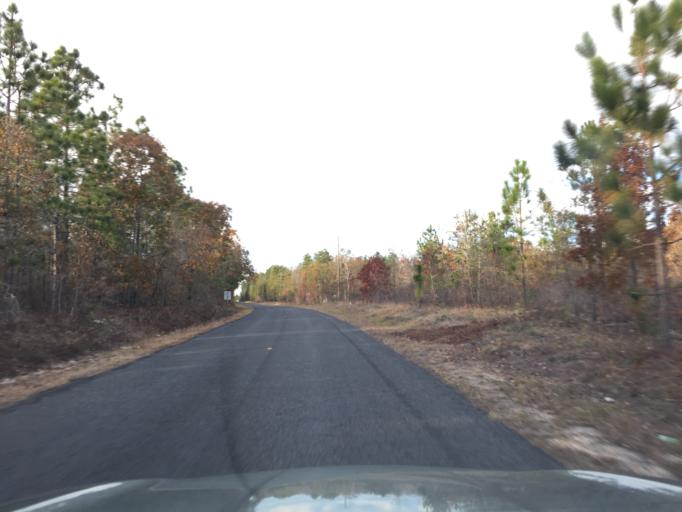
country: US
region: South Carolina
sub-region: Lexington County
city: Leesville
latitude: 33.6832
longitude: -81.3779
